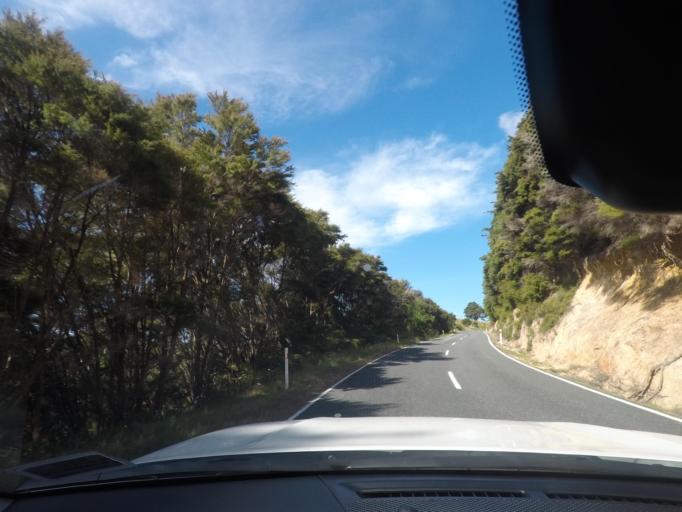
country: NZ
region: Northland
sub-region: Whangarei
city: Ngunguru
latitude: -35.6719
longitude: 174.4669
